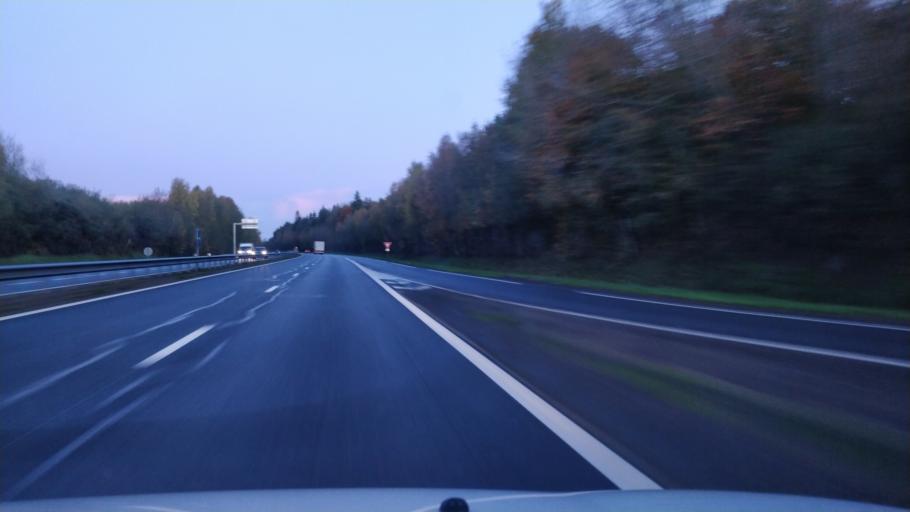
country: FR
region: Brittany
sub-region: Departement d'Ille-et-Vilaine
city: Saint-Meen-le-Grand
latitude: 48.1895
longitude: -2.2125
